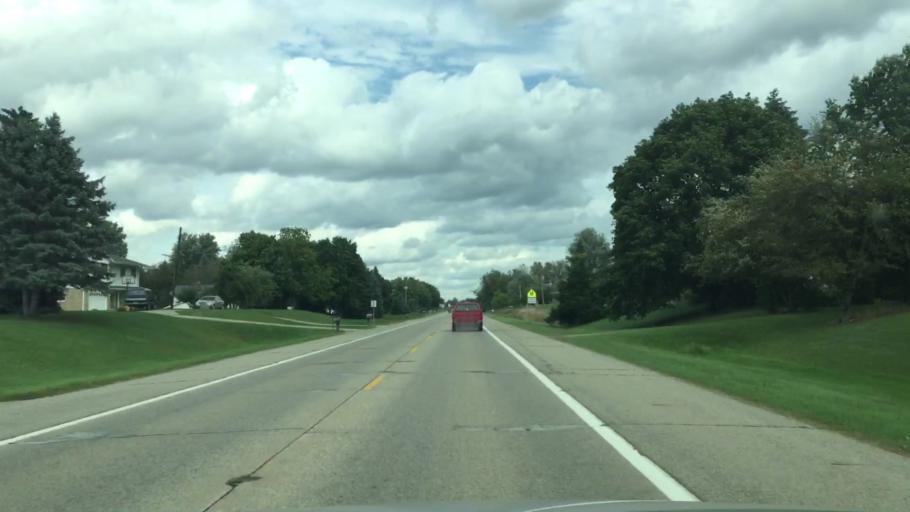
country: US
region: Michigan
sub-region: Shiawassee County
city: Owosso
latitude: 42.9625
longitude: -84.2012
